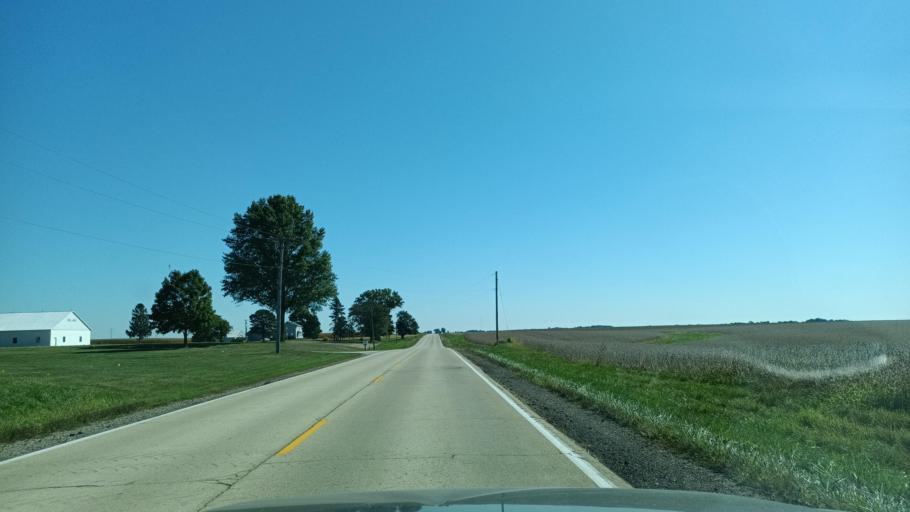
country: US
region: Illinois
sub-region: Peoria County
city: Elmwood
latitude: 40.9021
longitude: -89.9545
